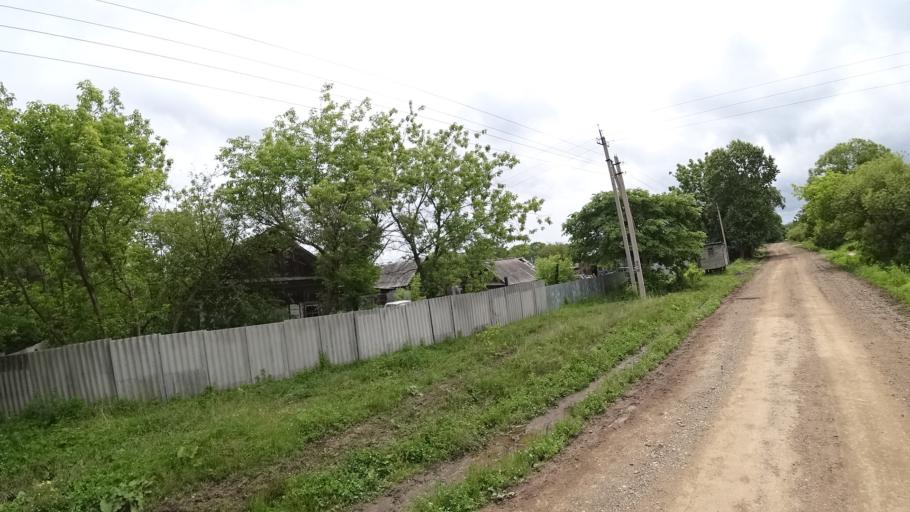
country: RU
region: Primorskiy
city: Novosysoyevka
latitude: 44.2279
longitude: 133.3731
